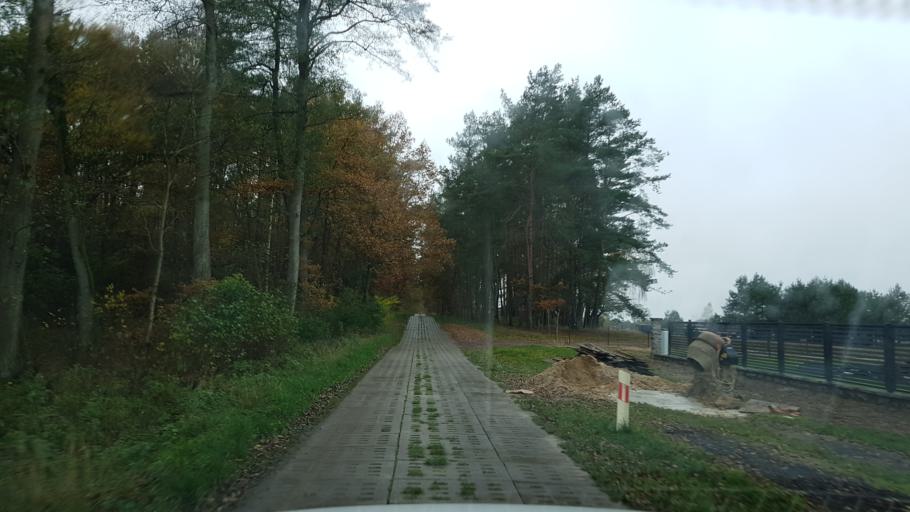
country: PL
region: West Pomeranian Voivodeship
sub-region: Powiat goleniowski
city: Goleniow
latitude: 53.5795
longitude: 14.7876
